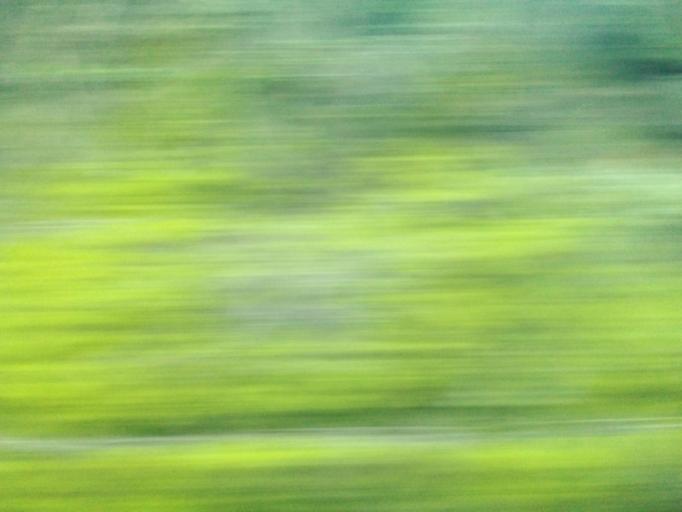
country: BR
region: Minas Gerais
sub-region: Rio Piracicaba
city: Rio Piracicaba
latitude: -19.8794
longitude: -43.1268
